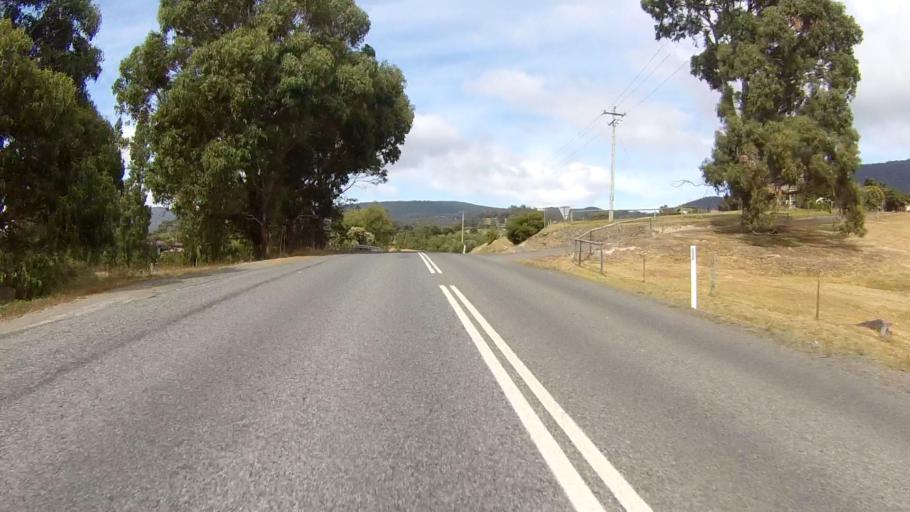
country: AU
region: Tasmania
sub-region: Kingborough
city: Kettering
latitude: -43.1528
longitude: 147.2388
